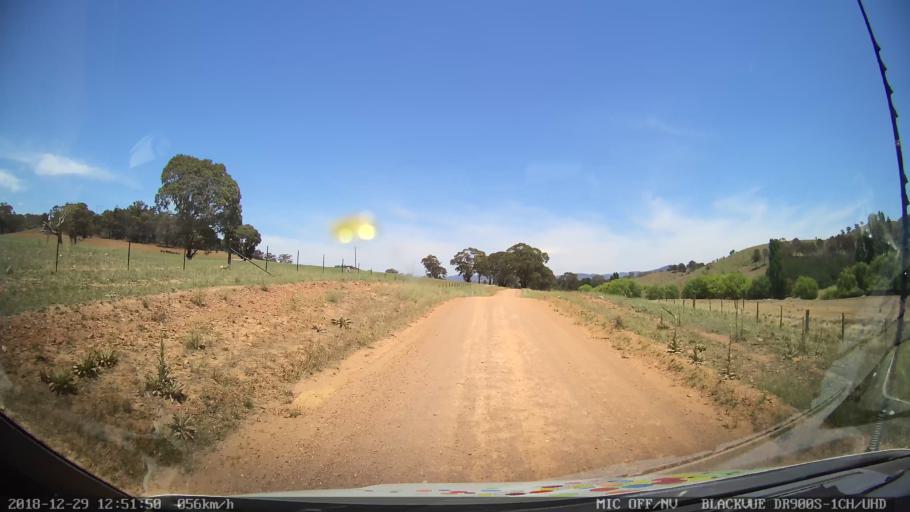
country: AU
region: Australian Capital Territory
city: Macarthur
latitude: -35.6774
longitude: 149.1969
